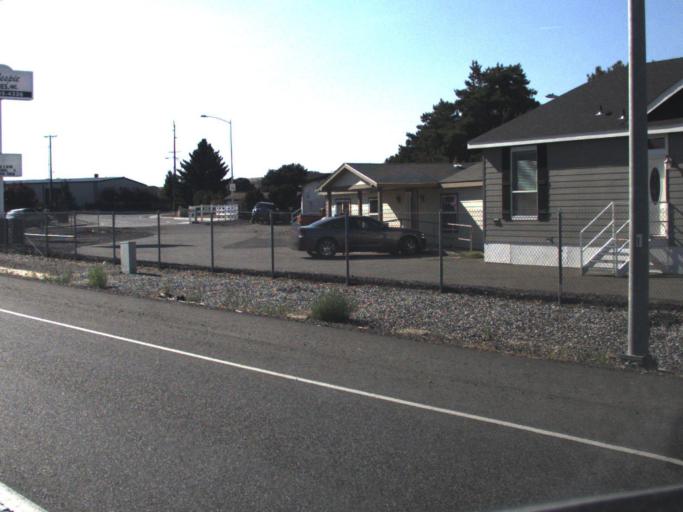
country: US
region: Washington
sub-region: Benton County
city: Kennewick
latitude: 46.1921
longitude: -119.1668
